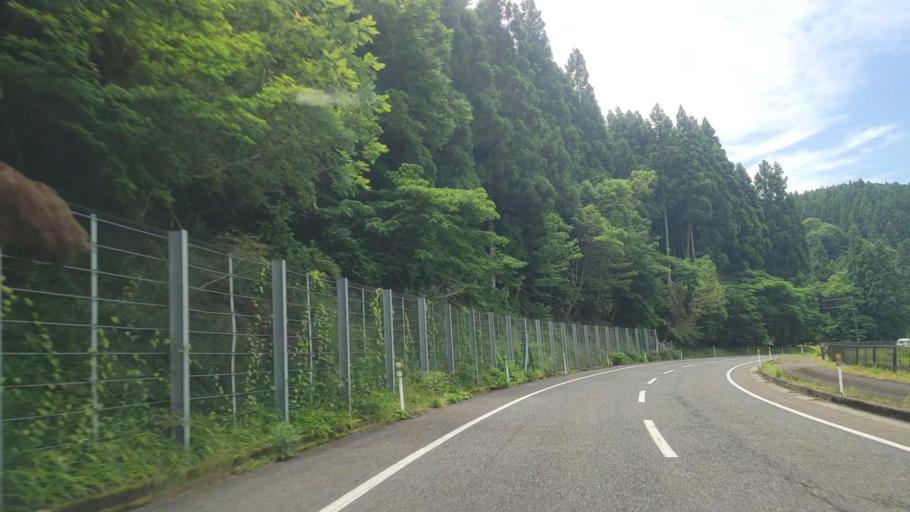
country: JP
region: Hyogo
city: Toyooka
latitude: 35.4908
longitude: 134.5614
